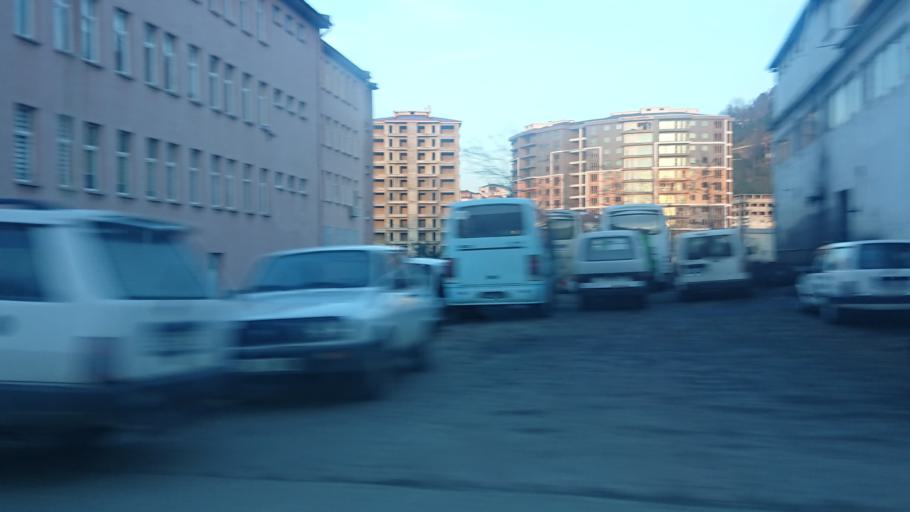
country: TR
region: Rize
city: Gundogdu
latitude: 41.0416
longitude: 40.5793
